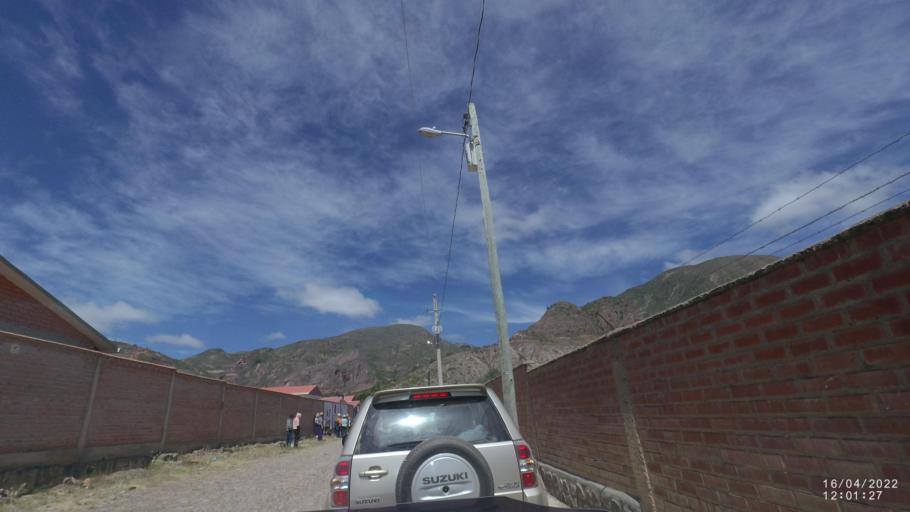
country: BO
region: Cochabamba
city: Mizque
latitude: -17.9864
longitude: -65.6286
